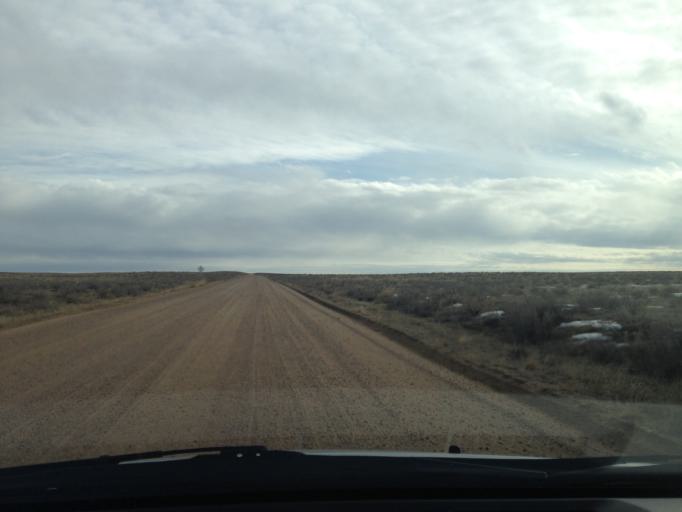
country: US
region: Colorado
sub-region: Weld County
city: Keenesburg
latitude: 40.2607
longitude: -104.2068
